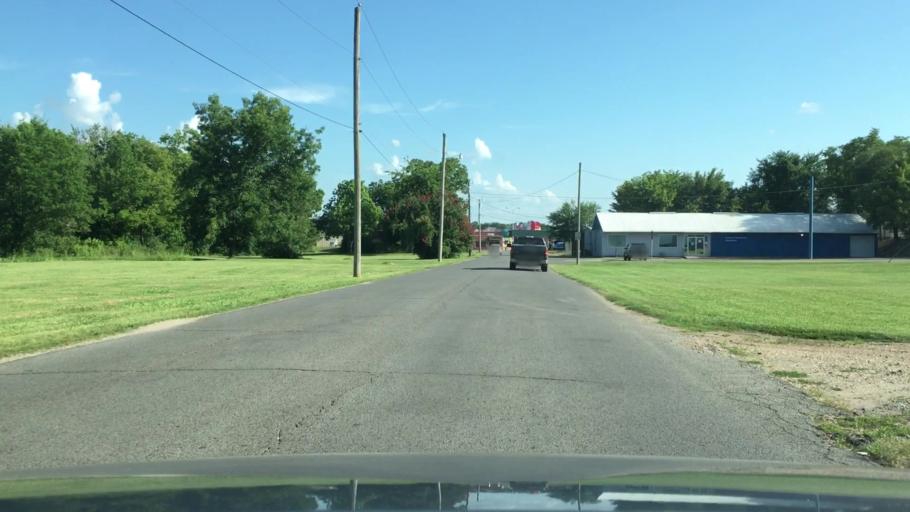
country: US
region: Oklahoma
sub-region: Cherokee County
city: Tahlequah
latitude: 35.9059
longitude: -94.9732
